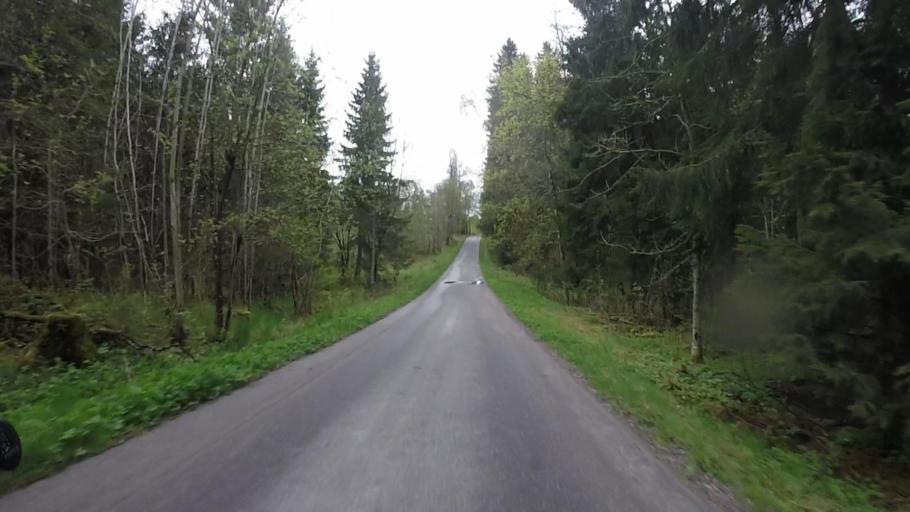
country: SE
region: Vaestra Goetaland
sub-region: Trollhattan
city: Sjuntorp
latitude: 58.2052
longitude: 12.2113
